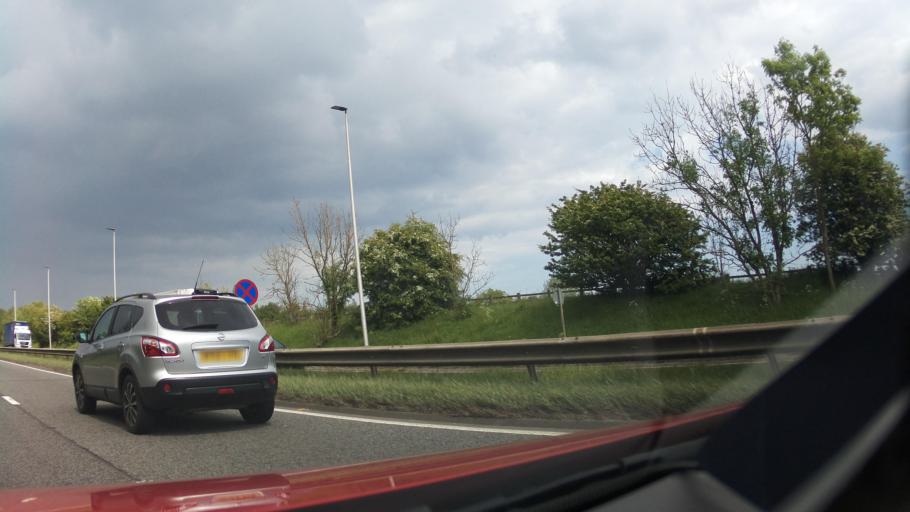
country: GB
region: England
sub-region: County Durham
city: Hawthorn
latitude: 54.7985
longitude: -1.3626
